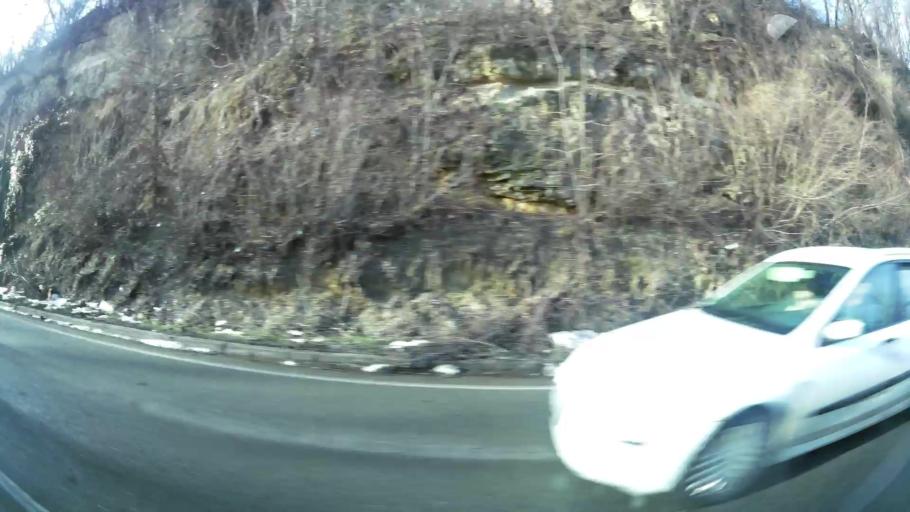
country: RS
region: Central Serbia
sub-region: Belgrade
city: Rakovica
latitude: 44.7216
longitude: 20.4342
